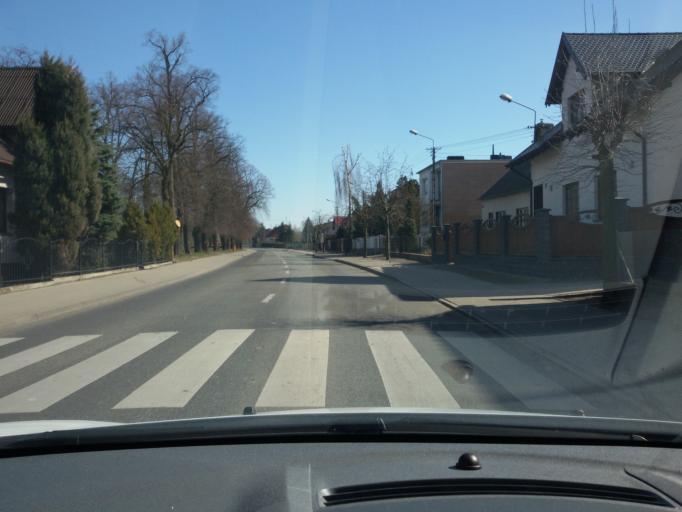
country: PL
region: Greater Poland Voivodeship
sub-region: Powiat gostynski
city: Poniec
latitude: 51.7620
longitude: 16.7966
